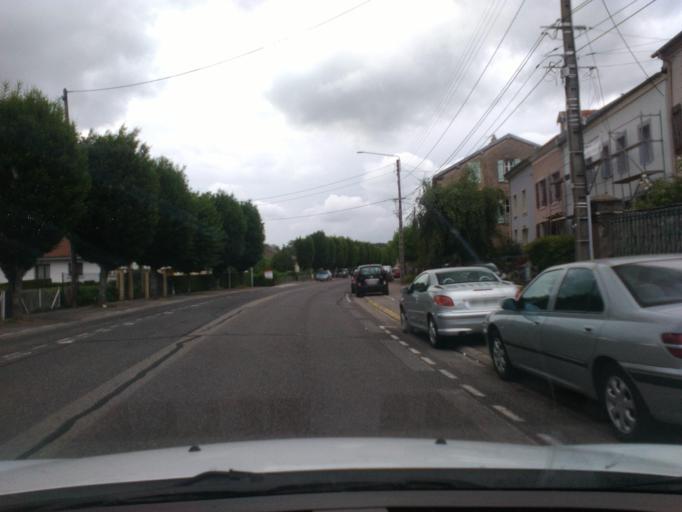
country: FR
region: Lorraine
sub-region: Departement de Meurthe-et-Moselle
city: Baccarat
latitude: 48.4440
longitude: 6.7479
